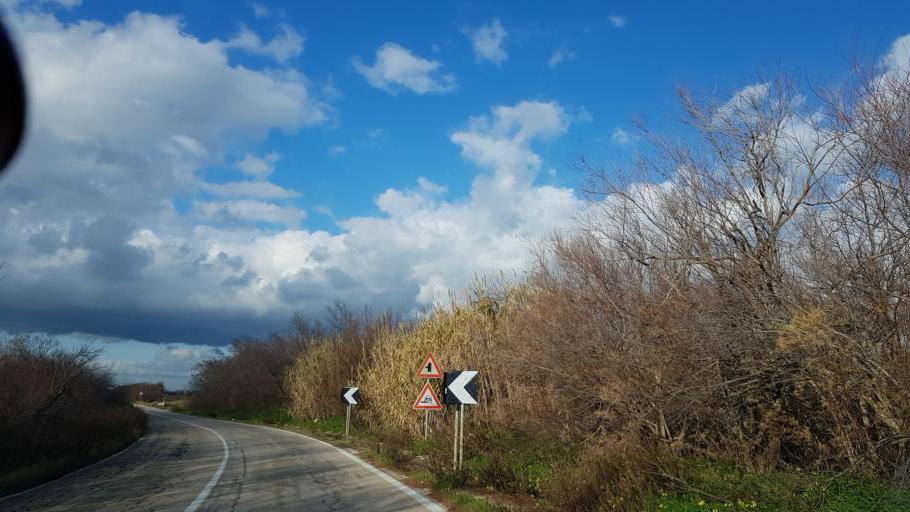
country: IT
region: Apulia
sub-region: Provincia di Brindisi
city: Materdomini
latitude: 40.6798
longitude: 17.9228
